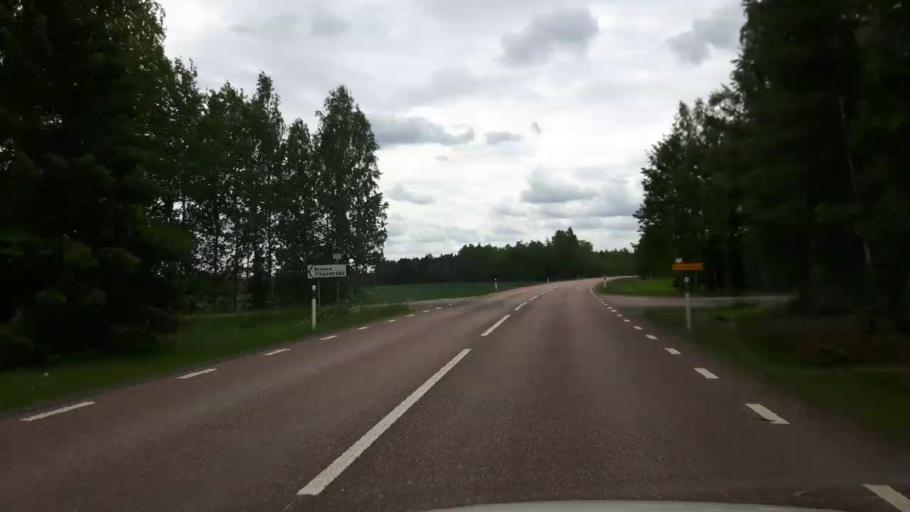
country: SE
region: Dalarna
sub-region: Hedemora Kommun
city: Brunna
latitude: 60.2520
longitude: 16.0099
